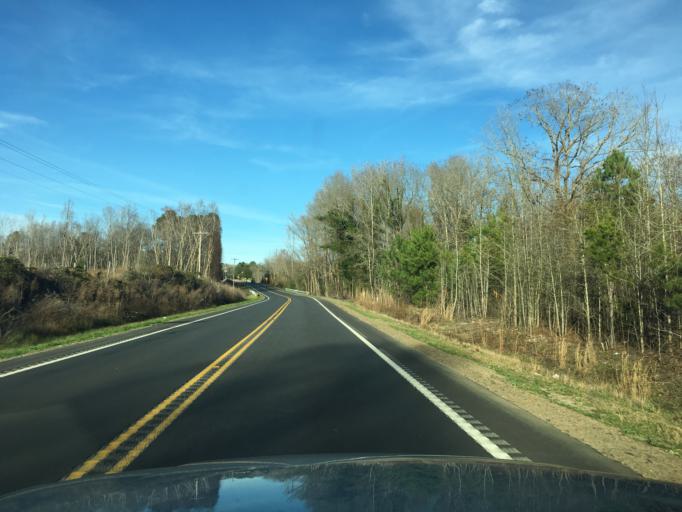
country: US
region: South Carolina
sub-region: Edgefield County
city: Johnston
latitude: 33.7281
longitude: -81.6548
